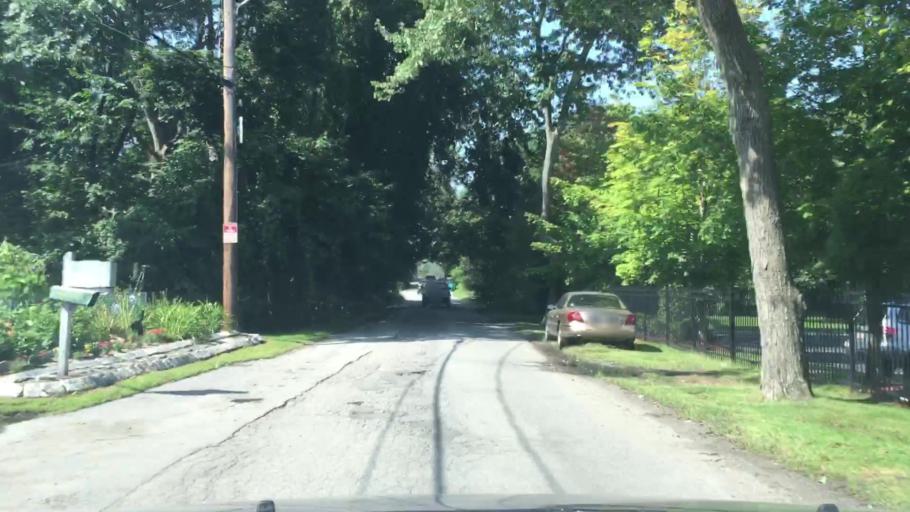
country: US
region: Massachusetts
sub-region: Middlesex County
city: Lowell
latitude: 42.6421
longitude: -71.3540
